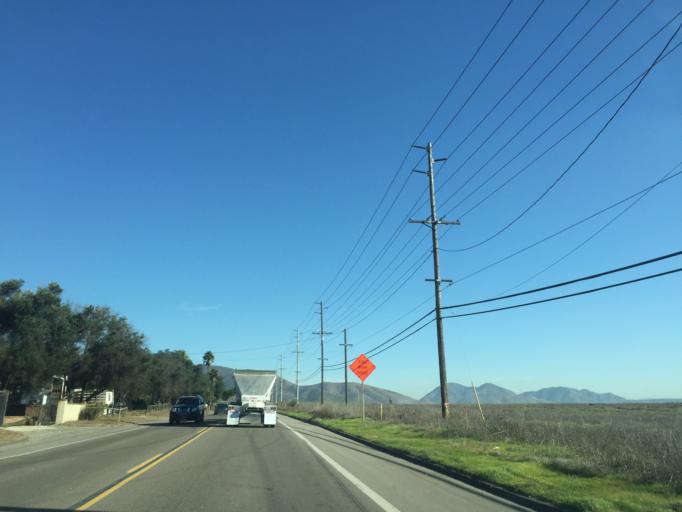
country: MX
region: Baja California
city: Tijuana
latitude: 32.5674
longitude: -116.9344
